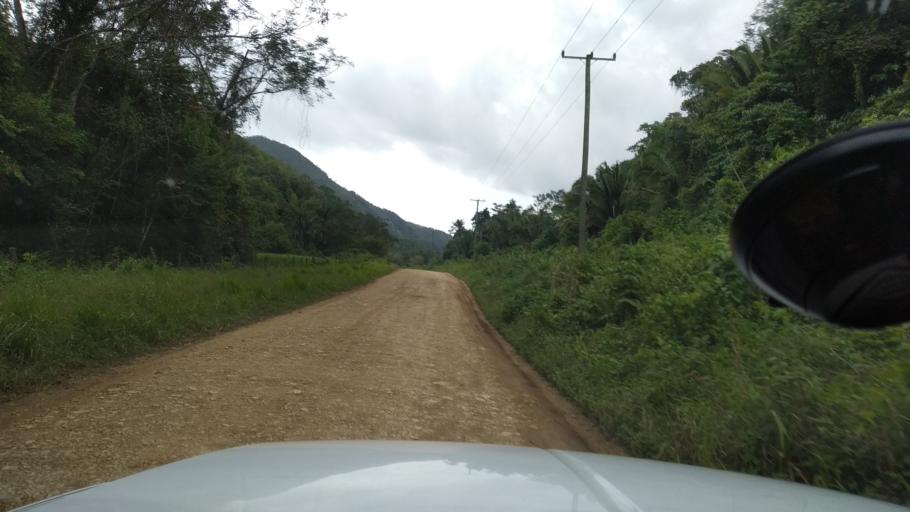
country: BZ
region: Toledo
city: Punta Gorda
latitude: 16.2078
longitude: -89.0263
